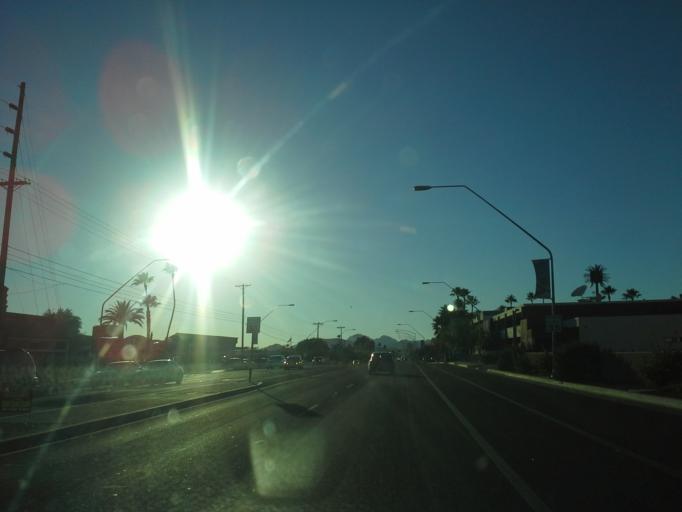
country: US
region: Arizona
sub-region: Pima County
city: Tucson
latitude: 32.2216
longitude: -110.9269
